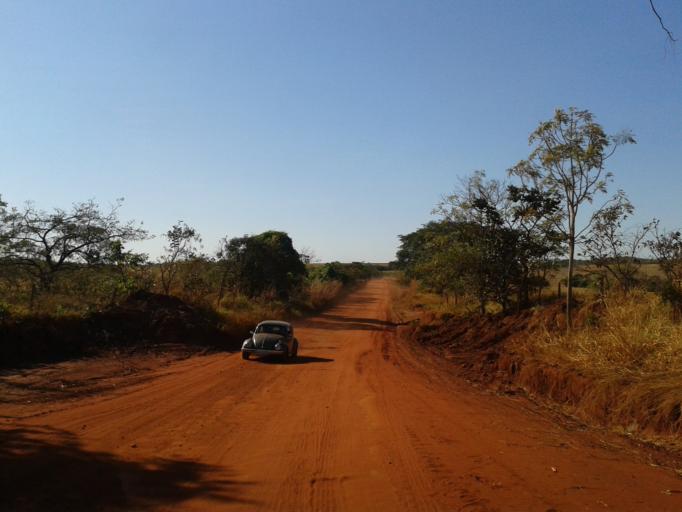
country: BR
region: Minas Gerais
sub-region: Ituiutaba
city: Ituiutaba
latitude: -18.9945
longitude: -49.3762
